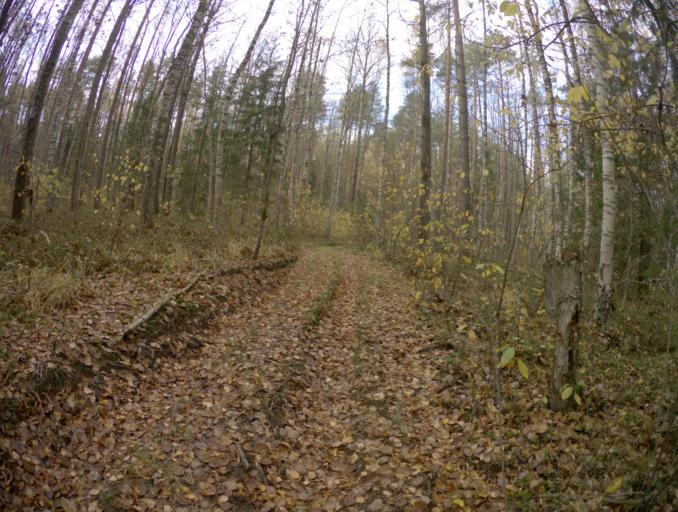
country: RU
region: Vladimir
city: Raduzhnyy
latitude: 55.9644
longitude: 40.3667
